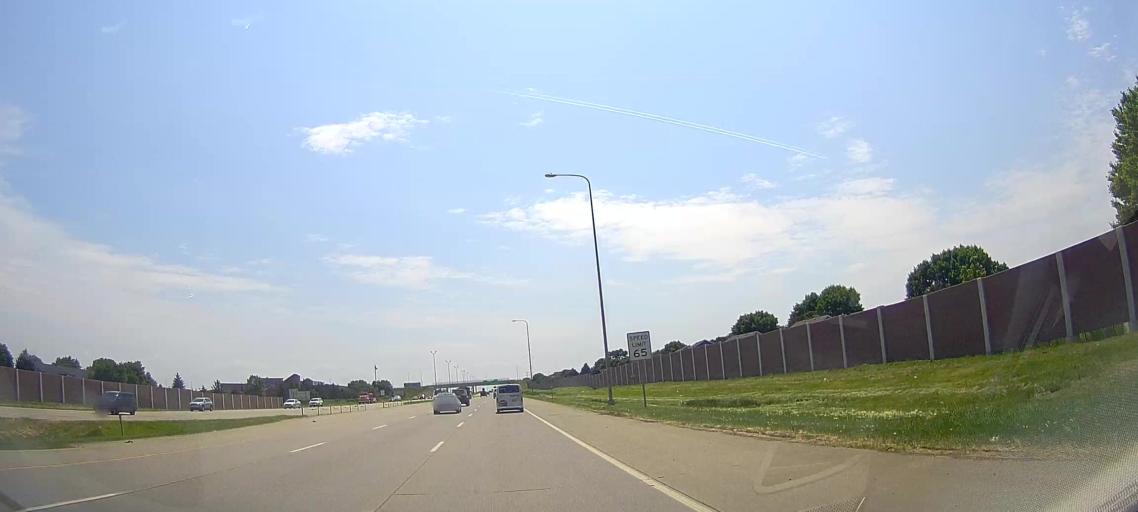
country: US
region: South Dakota
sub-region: Lincoln County
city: Tea
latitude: 43.5046
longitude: -96.7855
